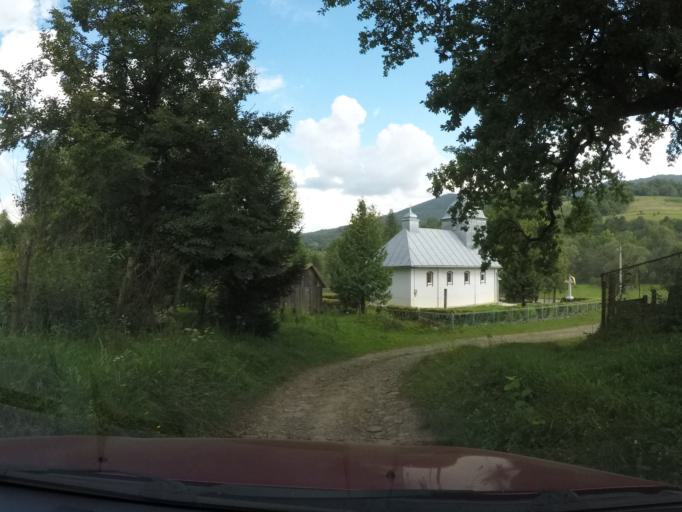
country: UA
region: Zakarpattia
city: Velykyi Bereznyi
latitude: 49.0293
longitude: 22.5910
